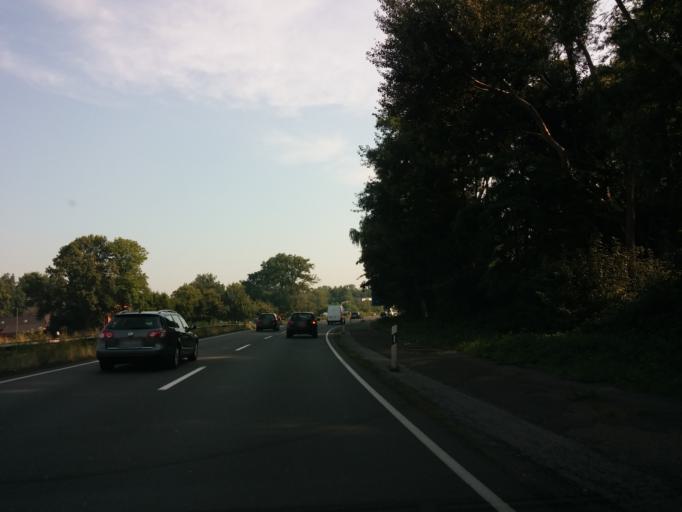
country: DE
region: North Rhine-Westphalia
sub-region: Regierungsbezirk Munster
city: Gladbeck
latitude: 51.5525
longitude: 6.9821
